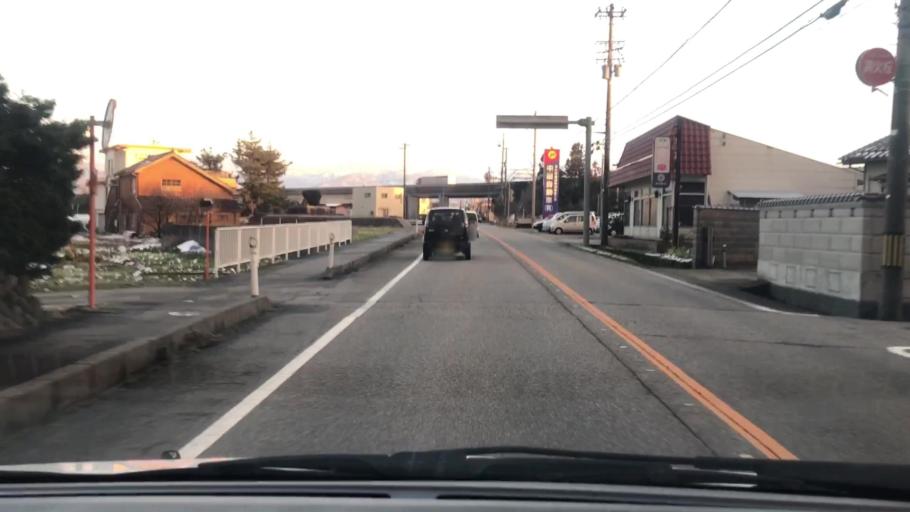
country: JP
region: Toyama
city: Kamiichi
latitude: 36.6701
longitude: 137.2903
